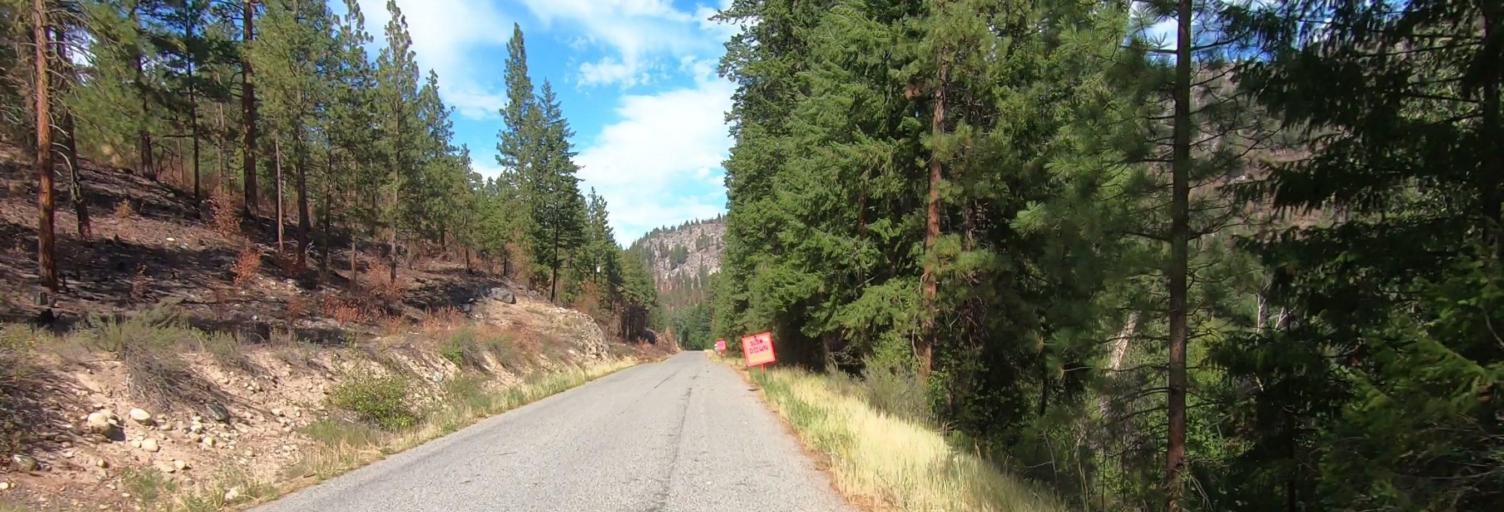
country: US
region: Washington
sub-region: Okanogan County
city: Brewster
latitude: 48.5883
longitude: -120.1691
